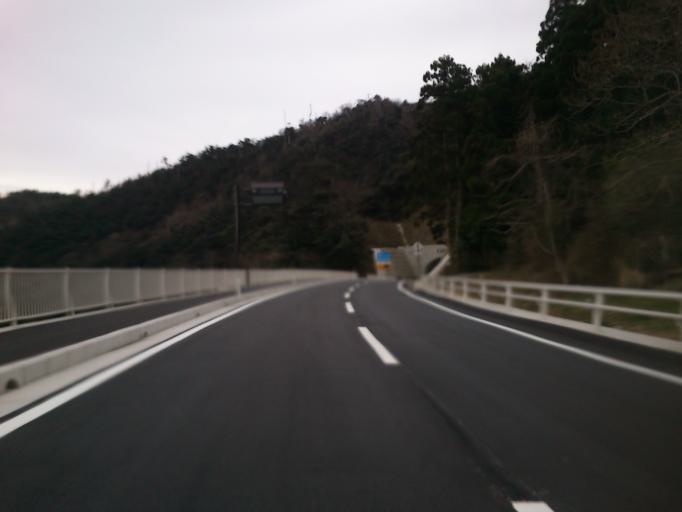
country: JP
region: Kyoto
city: Miyazu
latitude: 35.7455
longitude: 135.2553
